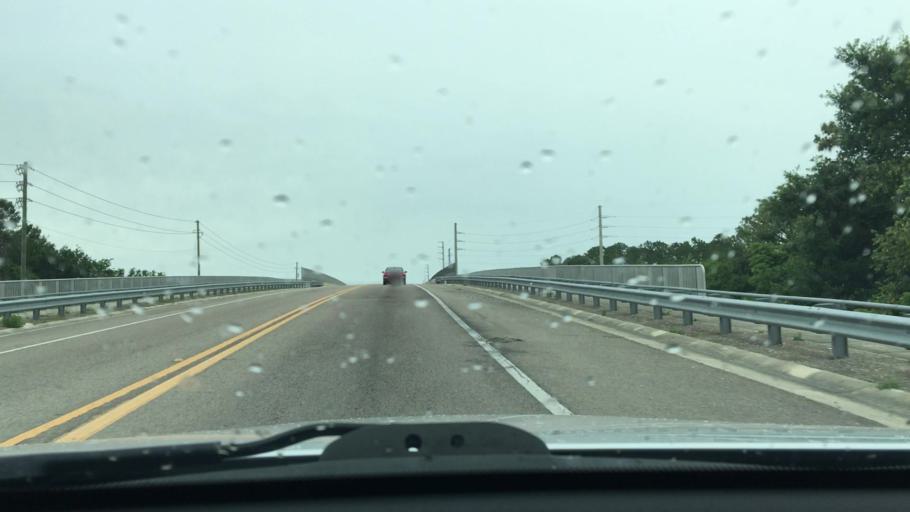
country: US
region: Florida
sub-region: Volusia County
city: Orange City
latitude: 28.9487
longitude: -81.2614
